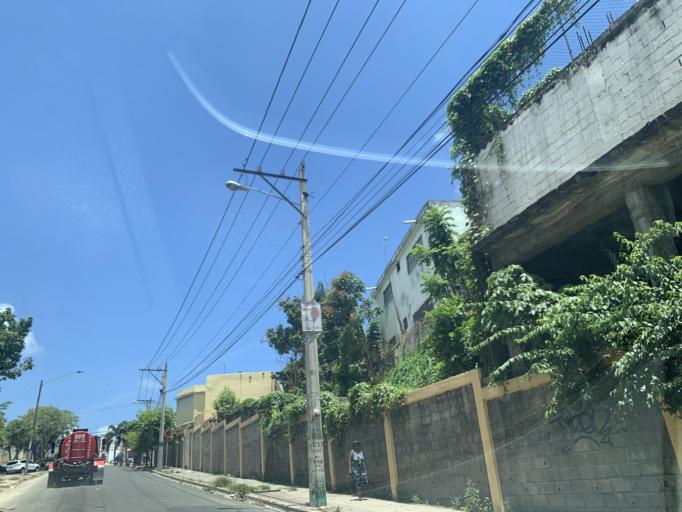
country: DO
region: Nacional
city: La Agustina
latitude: 18.4955
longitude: -69.9301
